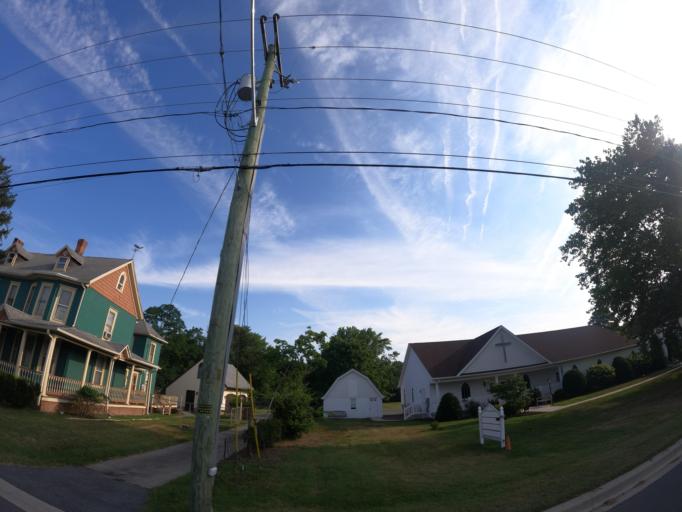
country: US
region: Delaware
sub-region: Sussex County
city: Ocean View
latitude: 38.5478
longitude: -75.1150
